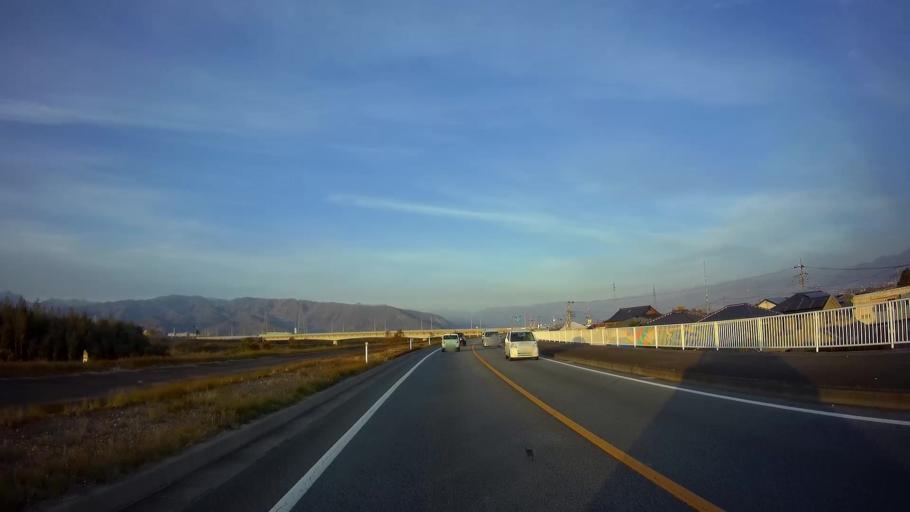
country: JP
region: Yamanashi
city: Kofu-shi
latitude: 35.6059
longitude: 138.5889
